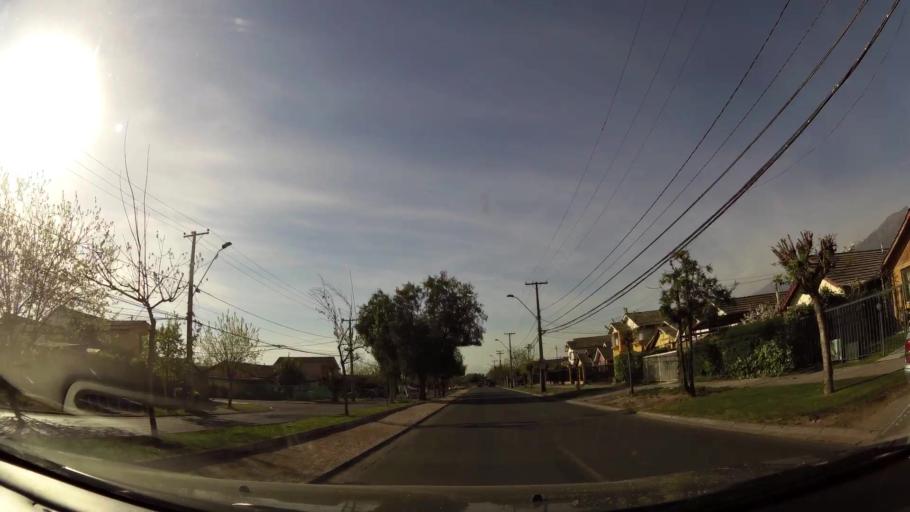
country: CL
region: Santiago Metropolitan
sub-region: Provincia de Cordillera
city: Puente Alto
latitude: -33.5825
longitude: -70.5635
